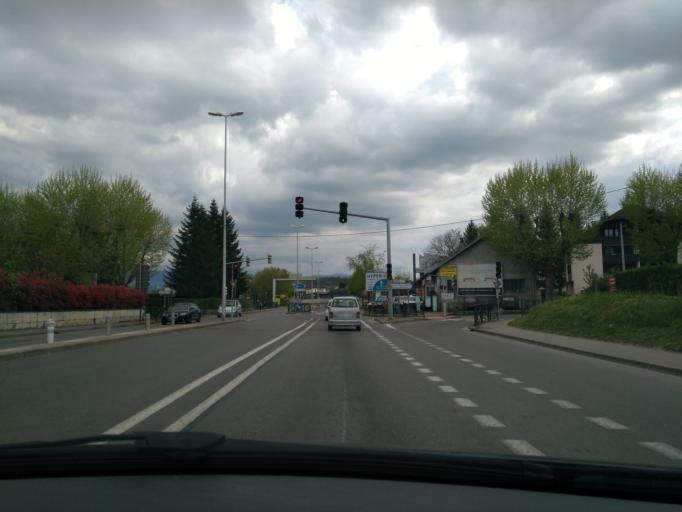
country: FR
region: Rhone-Alpes
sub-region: Departement de la Haute-Savoie
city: Rumilly
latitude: 45.8683
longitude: 5.9384
